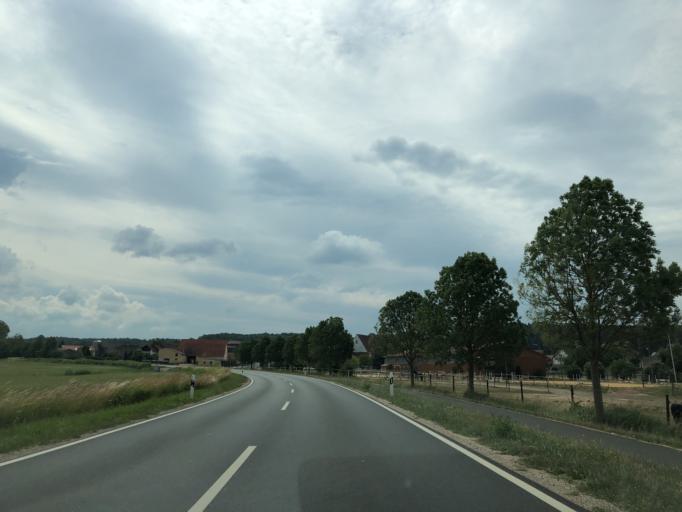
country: DE
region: Bavaria
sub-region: Regierungsbezirk Mittelfranken
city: Muhlhausen
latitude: 49.7461
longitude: 10.7770
